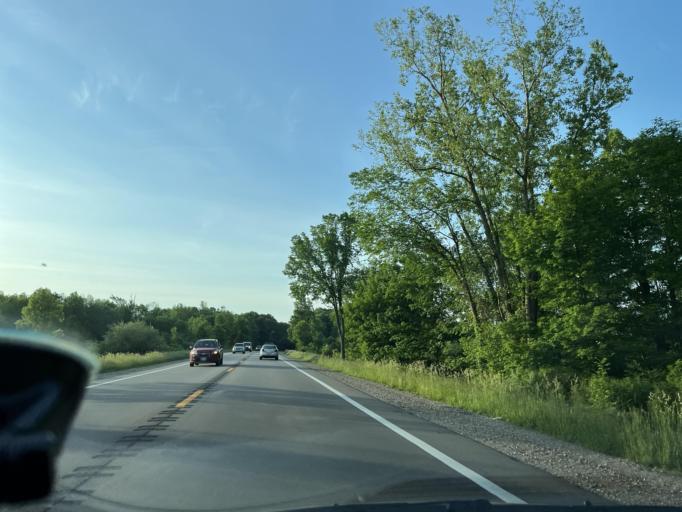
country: US
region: Michigan
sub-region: Barry County
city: Middleville
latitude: 42.7458
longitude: -85.4941
